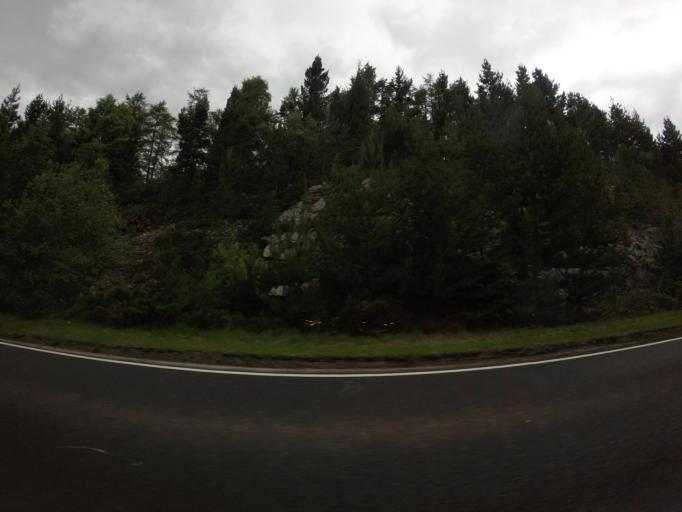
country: GB
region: Scotland
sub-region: Highland
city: Muir of Ord
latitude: 57.6309
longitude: -4.6886
